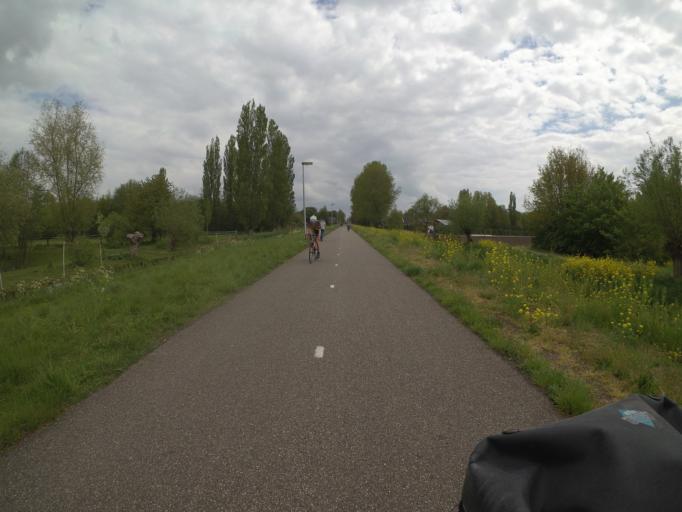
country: NL
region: North Brabant
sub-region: Gemeente Waalwijk
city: Waspik
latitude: 51.6844
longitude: 4.9306
